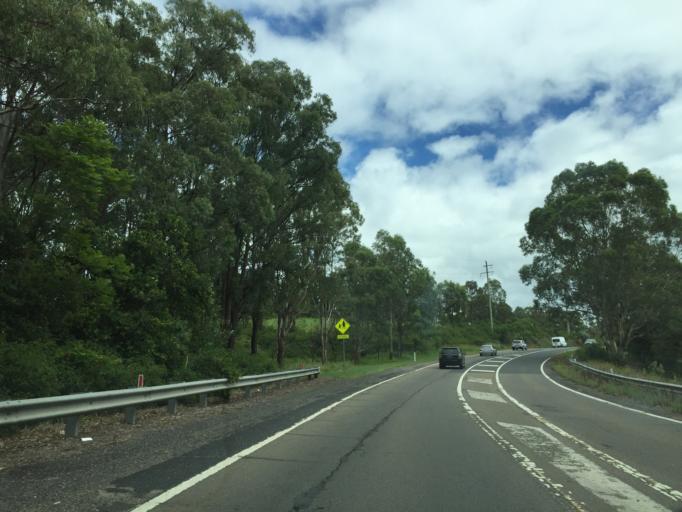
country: AU
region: New South Wales
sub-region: Hawkesbury
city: Richmond
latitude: -33.5715
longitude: 150.7073
